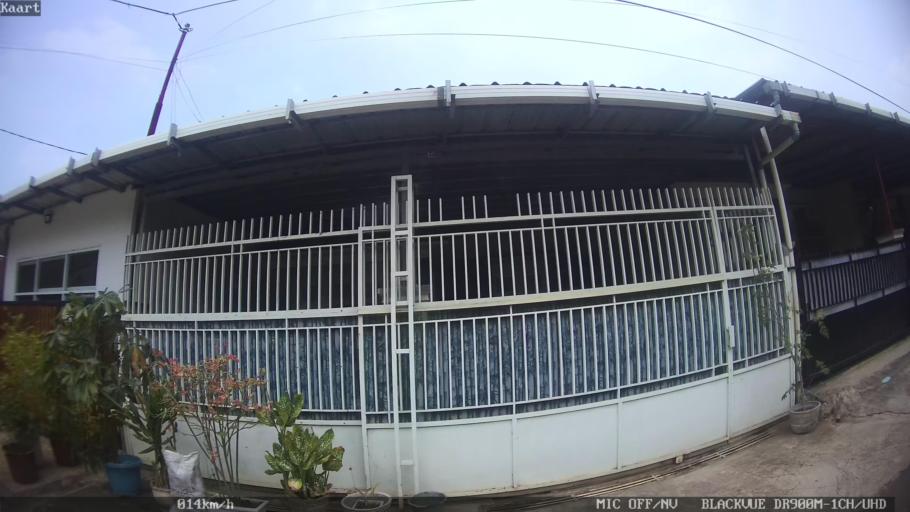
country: ID
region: Lampung
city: Bandarlampung
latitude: -5.4177
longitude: 105.2772
